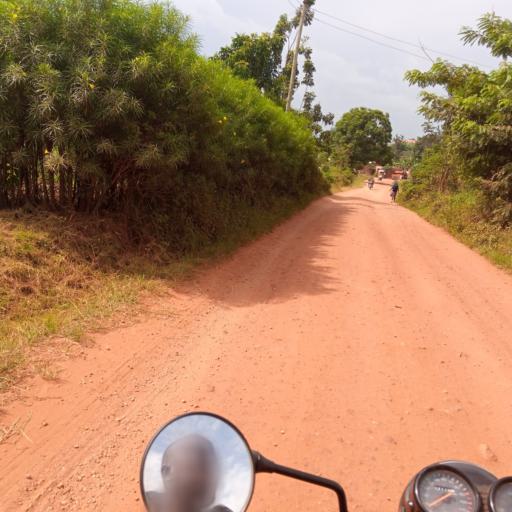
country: UG
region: Eastern Region
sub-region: Mbale District
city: Mbale
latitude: 1.0952
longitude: 34.1898
